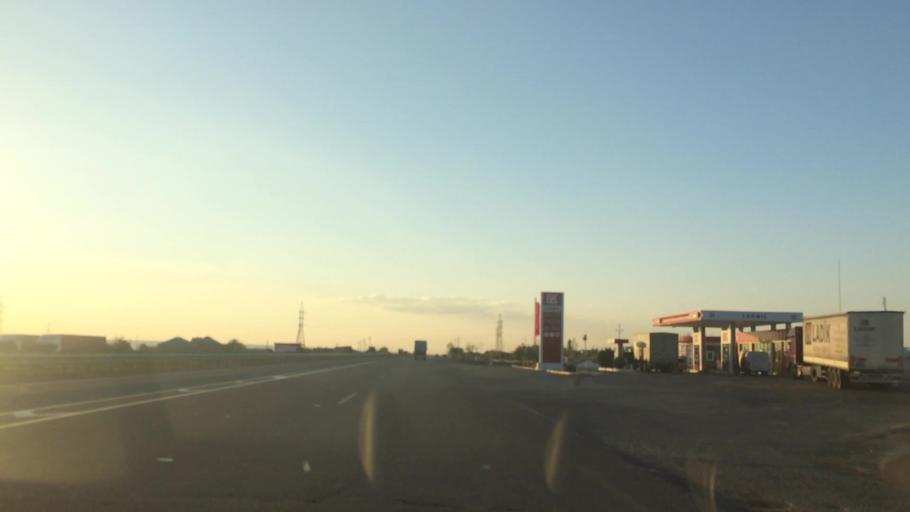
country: AZ
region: Baki
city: Qobustan
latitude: 39.9683
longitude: 49.2709
